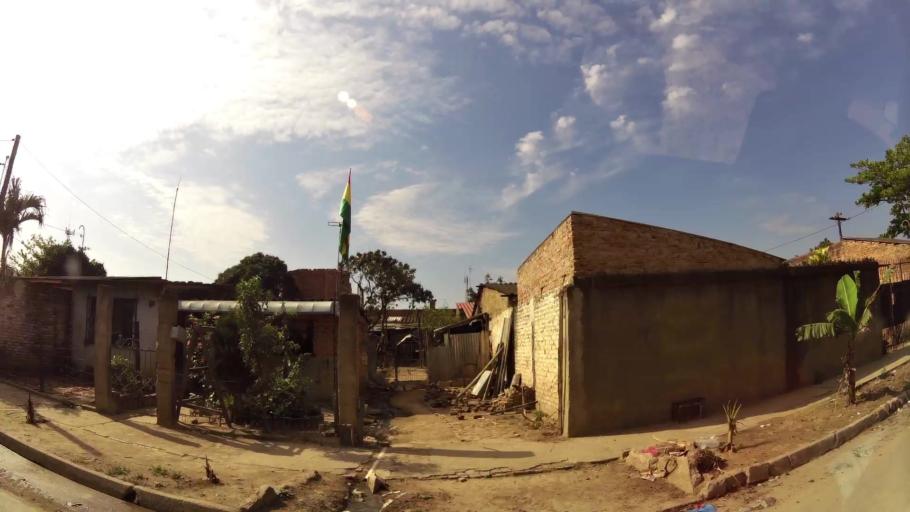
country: BO
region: Santa Cruz
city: Santa Cruz de la Sierra
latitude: -17.7258
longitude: -63.1395
